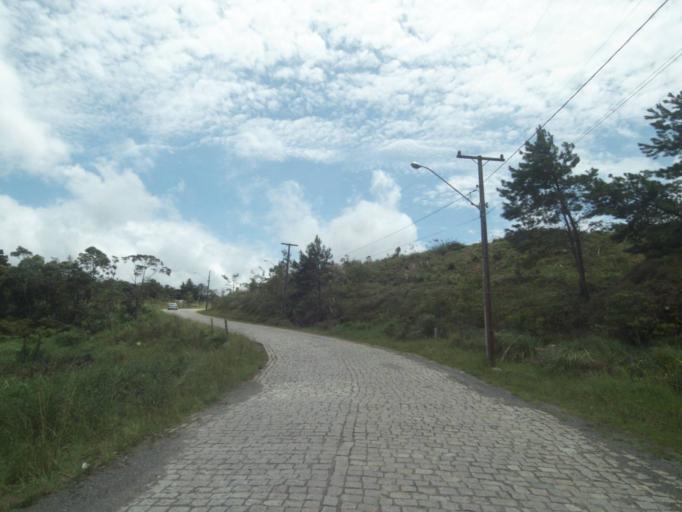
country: BR
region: Parana
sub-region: Campina Grande Do Sul
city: Campina Grande do Sul
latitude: -25.1075
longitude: -48.8058
